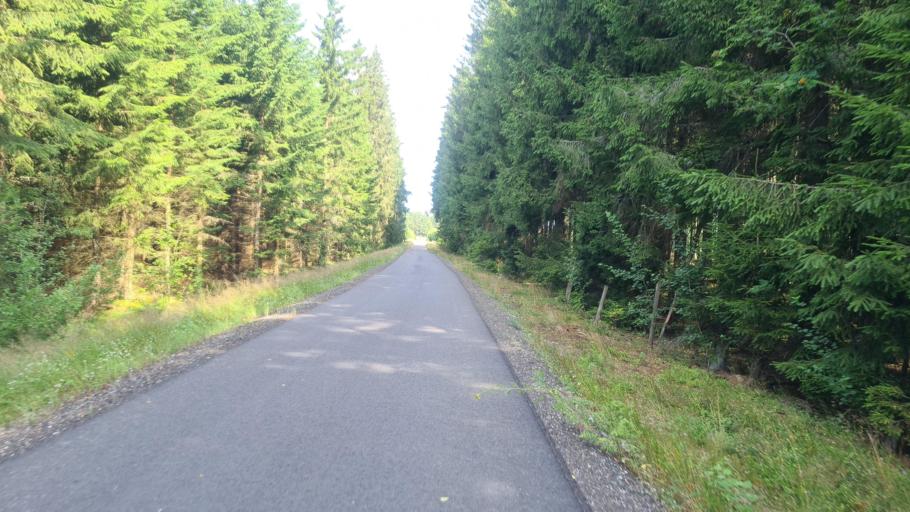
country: SE
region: Kronoberg
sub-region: Ljungby Kommun
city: Ljungby
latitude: 56.8620
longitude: 13.9779
